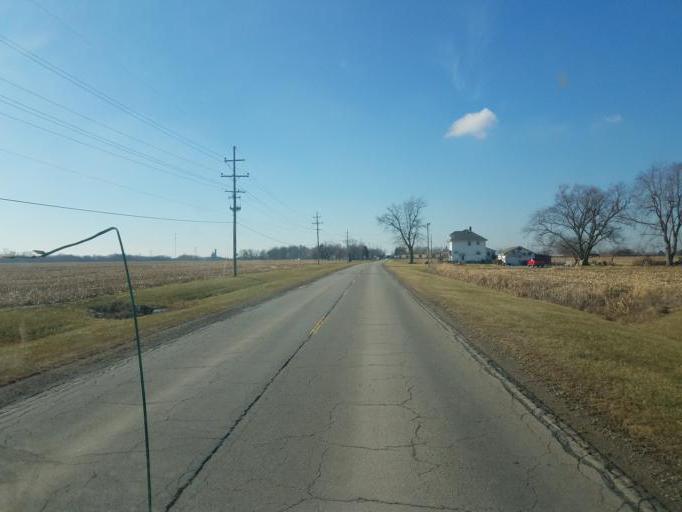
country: US
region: Ohio
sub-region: Marion County
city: Marion
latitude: 40.6294
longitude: -83.1101
